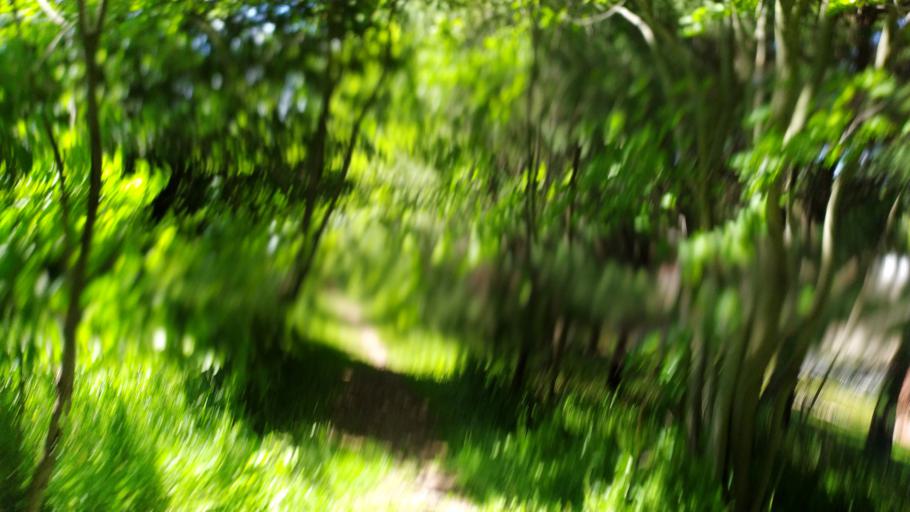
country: CA
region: Ontario
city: Stratford
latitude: 43.3679
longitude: -81.0050
